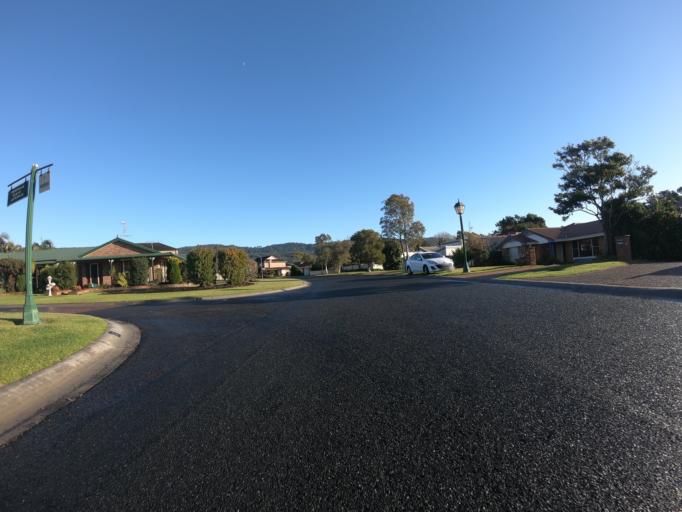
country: AU
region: New South Wales
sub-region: Wollongong
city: Bulli
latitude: -34.3568
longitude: 150.9152
